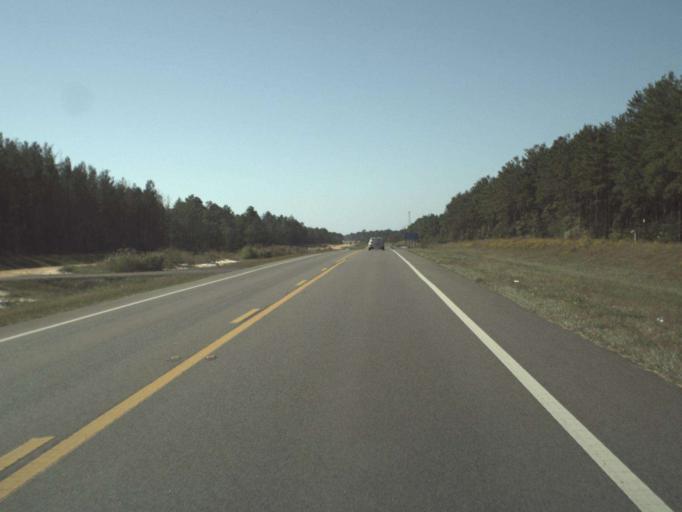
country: US
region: Florida
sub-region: Walton County
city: Freeport
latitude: 30.5079
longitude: -86.1143
